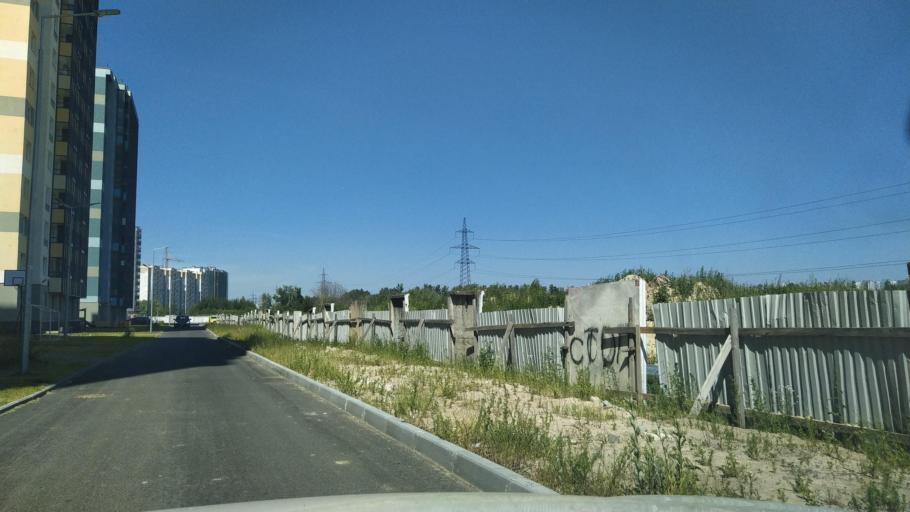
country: RU
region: St.-Petersburg
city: Krasnogvargeisky
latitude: 60.0004
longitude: 30.4541
